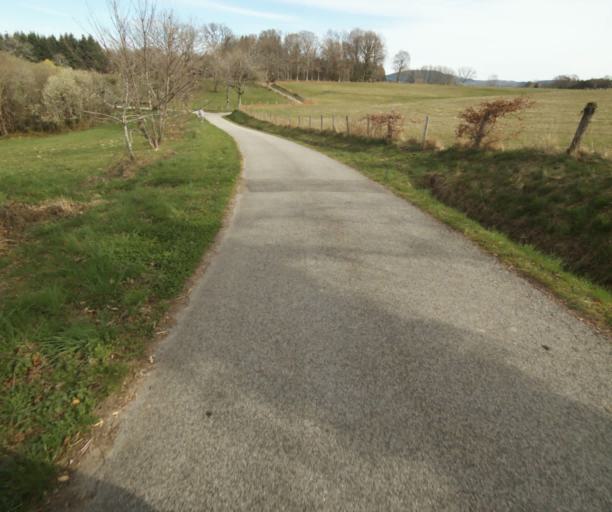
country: FR
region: Limousin
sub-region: Departement de la Correze
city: Correze
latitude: 45.4175
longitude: 1.8150
